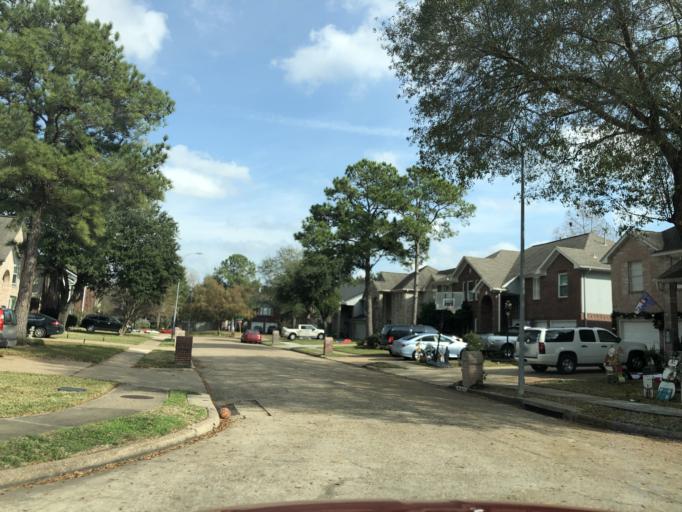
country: US
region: Texas
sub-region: Harris County
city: Tomball
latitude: 30.0401
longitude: -95.5441
